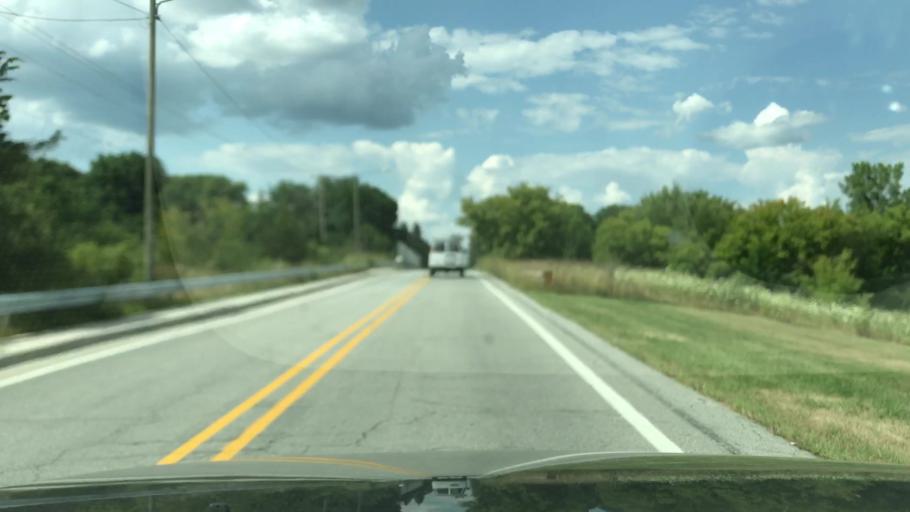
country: US
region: Michigan
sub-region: Kent County
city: East Grand Rapids
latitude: 42.9756
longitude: -85.6104
